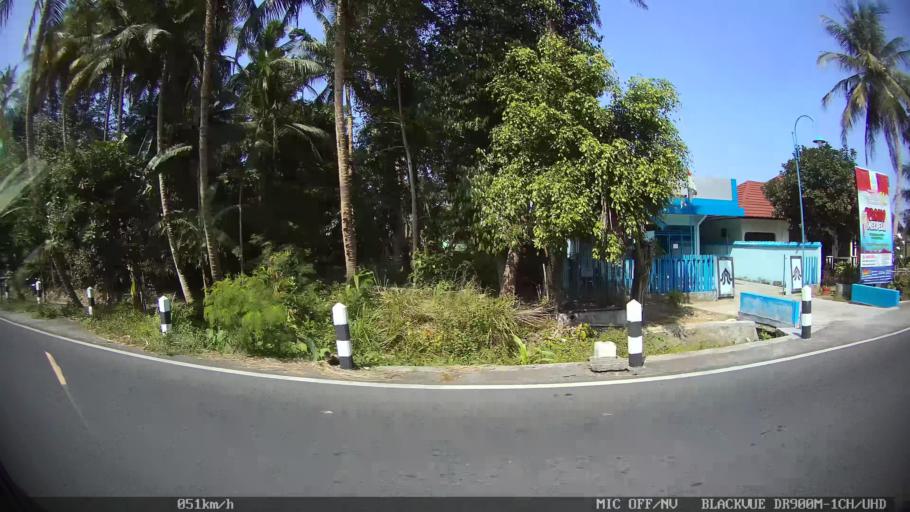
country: ID
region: Daerah Istimewa Yogyakarta
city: Srandakan
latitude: -7.9368
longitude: 110.2230
